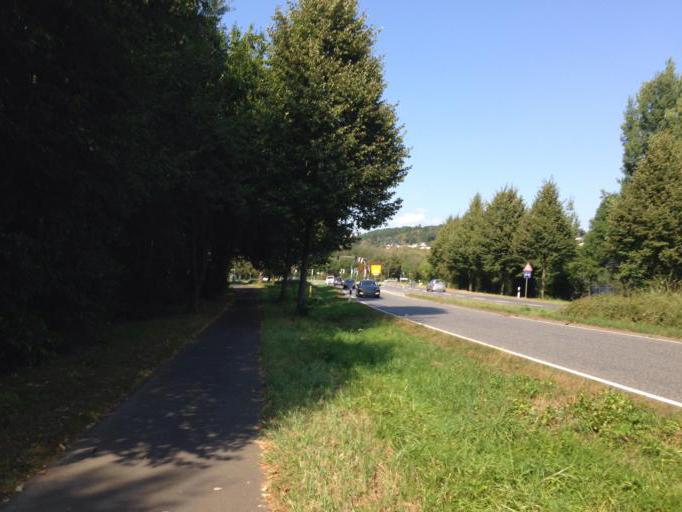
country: DE
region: Hesse
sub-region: Regierungsbezirk Giessen
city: Heuchelheim
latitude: 50.6089
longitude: 8.6509
